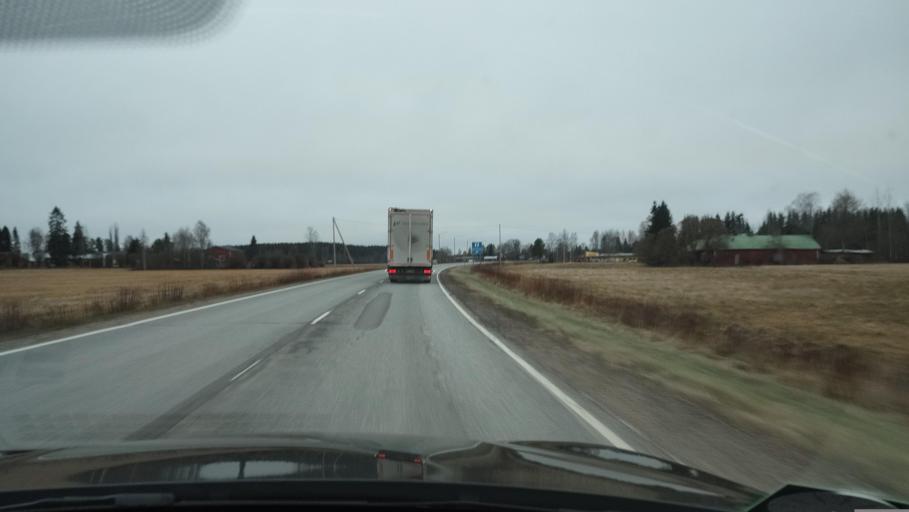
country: FI
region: Southern Ostrobothnia
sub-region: Suupohja
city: Kauhajoki
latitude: 62.3588
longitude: 22.0689
